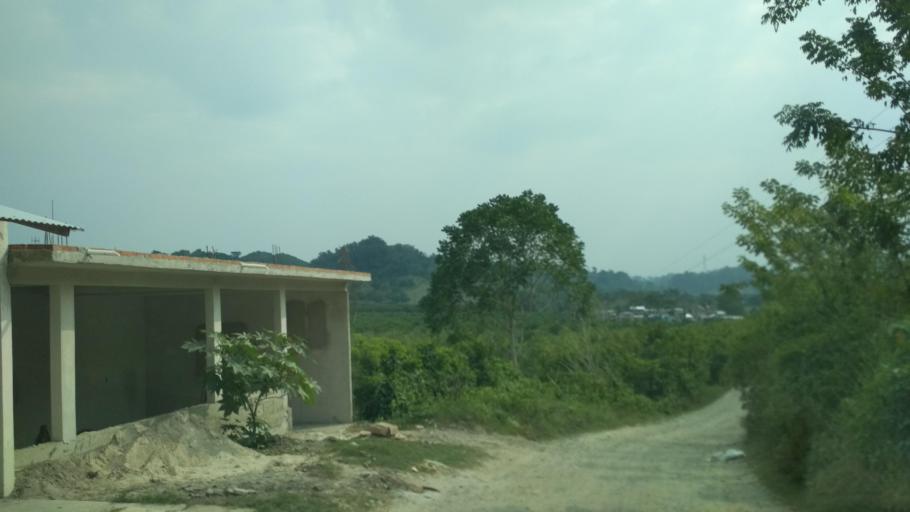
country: MM
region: Kayah
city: Loikaw
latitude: 20.2347
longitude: 97.2785
